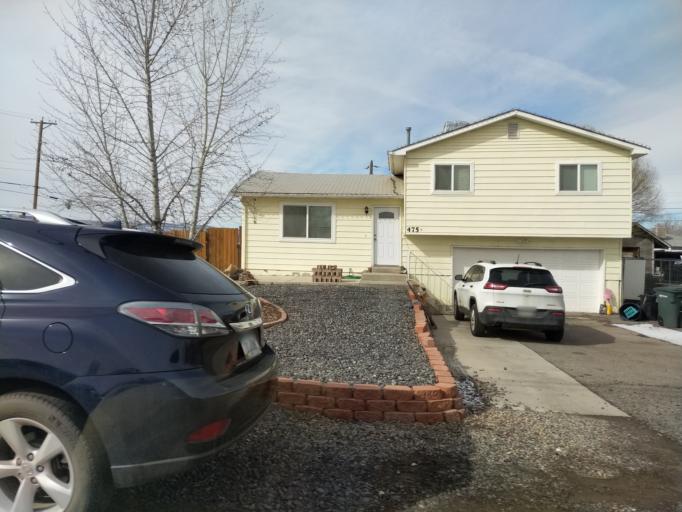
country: US
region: Colorado
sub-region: Mesa County
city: Grand Junction
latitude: 39.0740
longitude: -108.5244
